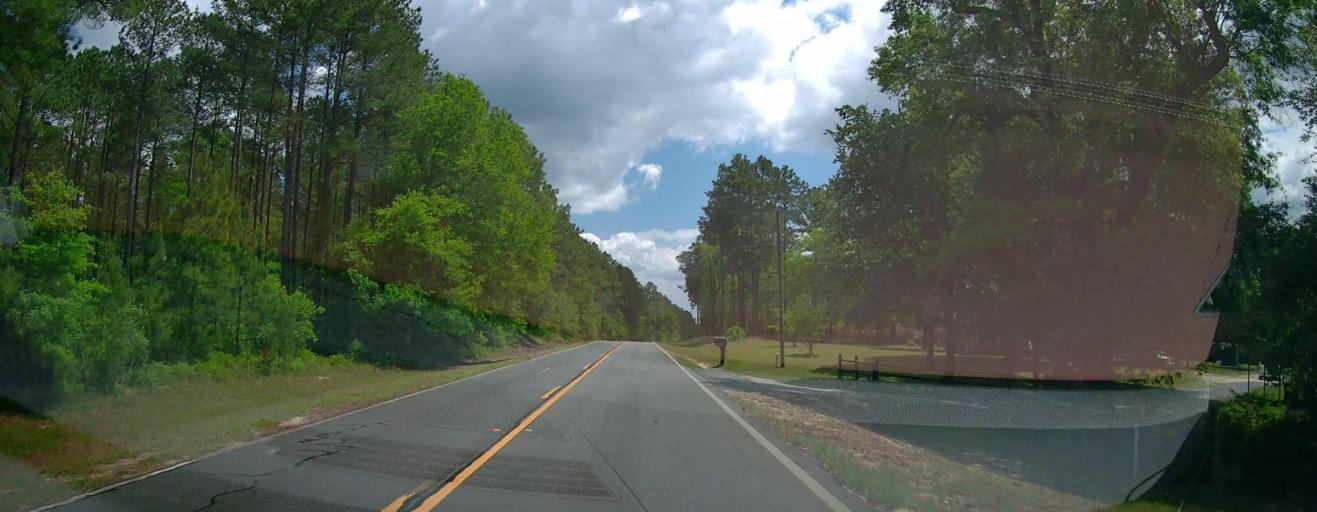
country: US
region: Georgia
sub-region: Treutlen County
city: Soperton
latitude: 32.4972
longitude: -82.6112
